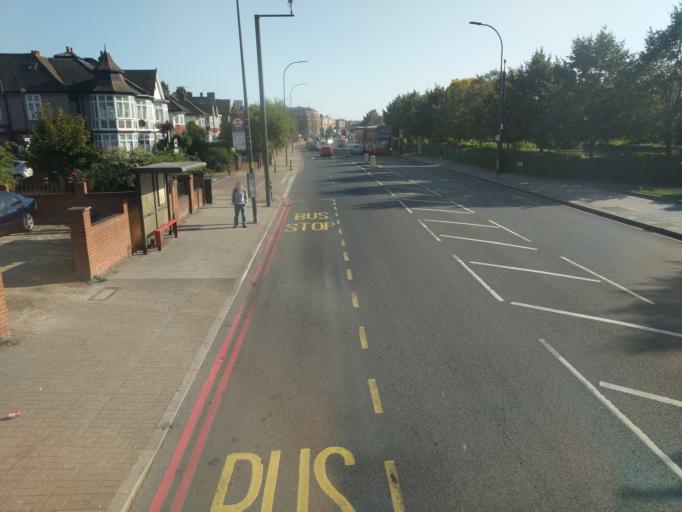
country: GB
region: England
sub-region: Greater London
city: Catford
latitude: 51.4373
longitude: -0.0186
